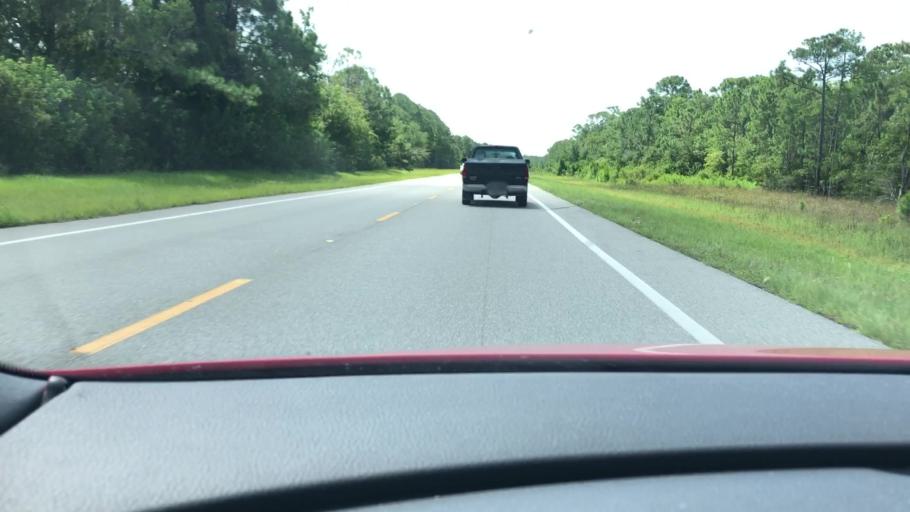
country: US
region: Florida
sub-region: Volusia County
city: South Daytona
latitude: 29.1492
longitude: -81.0618
